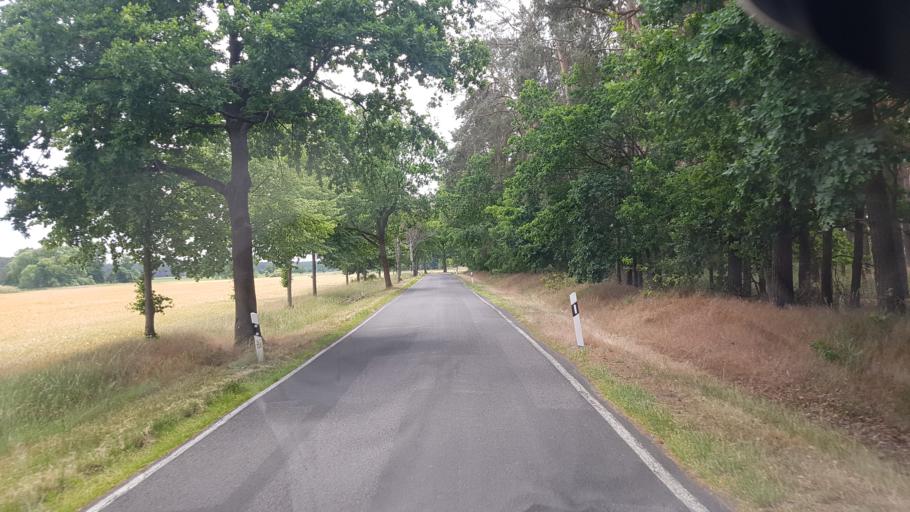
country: DE
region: Brandenburg
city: Ihlow
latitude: 51.8265
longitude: 13.2362
